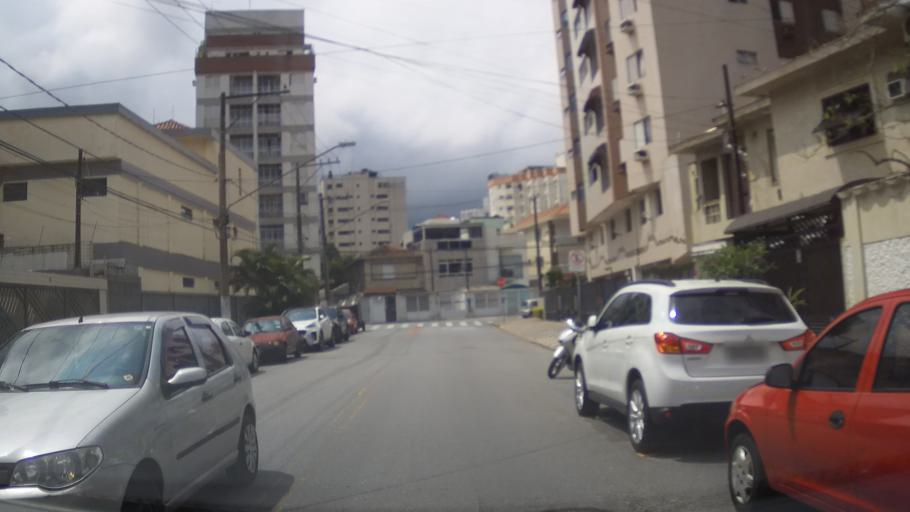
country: BR
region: Sao Paulo
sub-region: Santos
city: Santos
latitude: -23.9657
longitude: -46.3157
